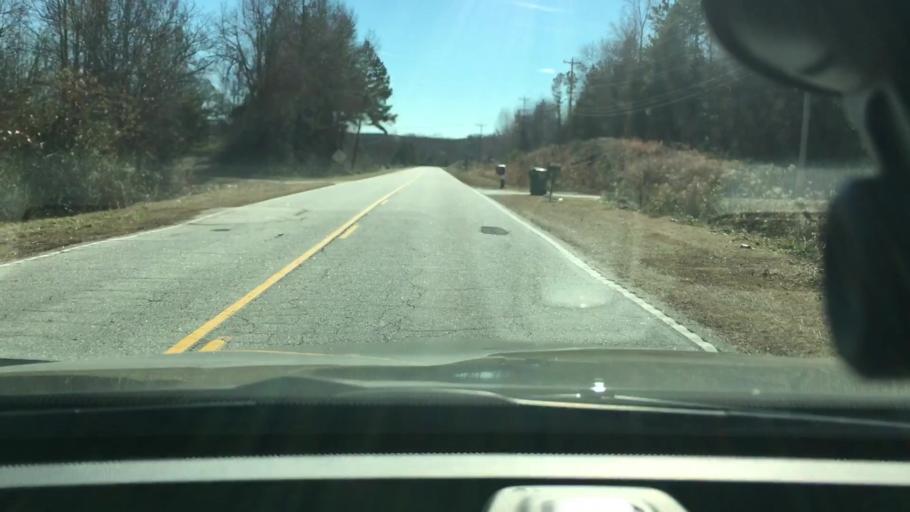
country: US
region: South Carolina
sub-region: Cherokee County
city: Gaffney
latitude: 34.9987
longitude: -81.6921
